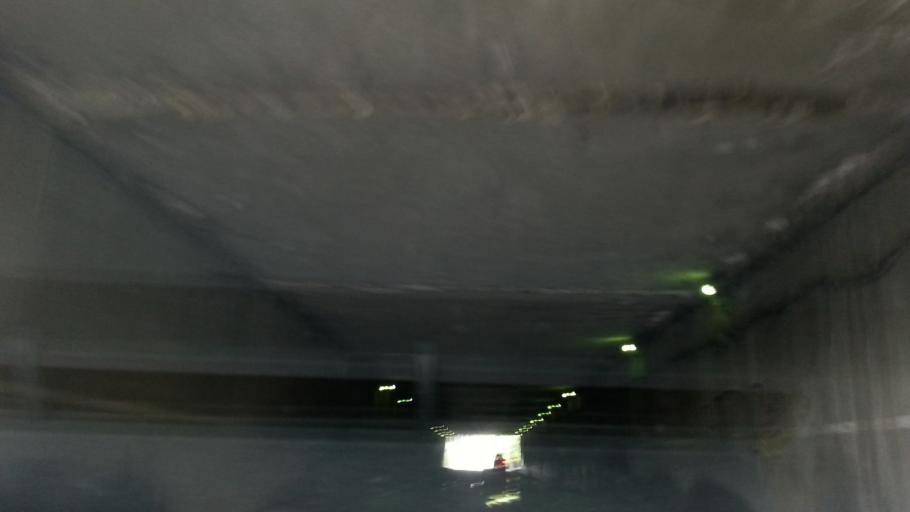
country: RS
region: Central Serbia
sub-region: Belgrade
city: Savski Venac
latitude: 44.7724
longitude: 20.4377
